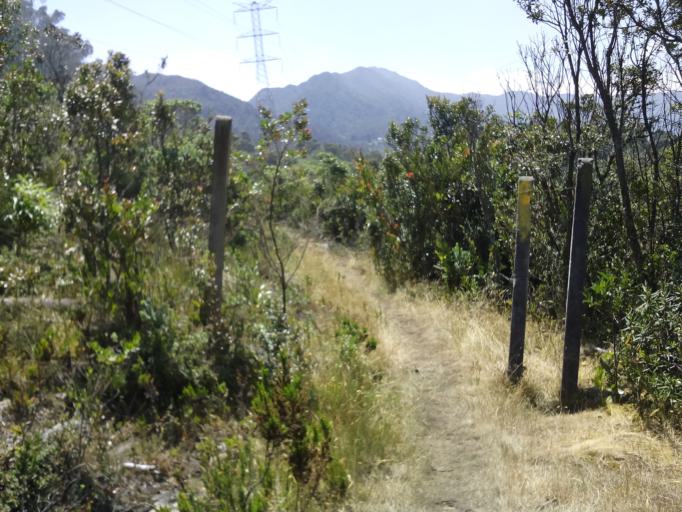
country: CO
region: Bogota D.C.
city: Bogota
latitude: 4.6083
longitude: -74.0370
